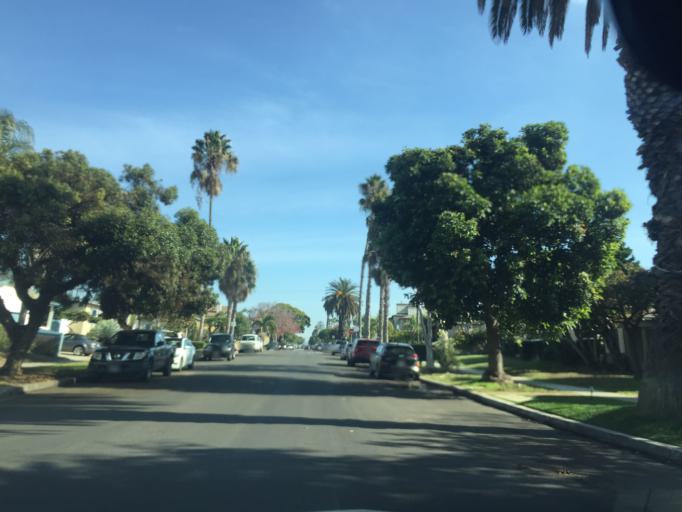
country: US
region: California
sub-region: San Diego County
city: La Jolla
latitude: 32.7951
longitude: -117.2483
